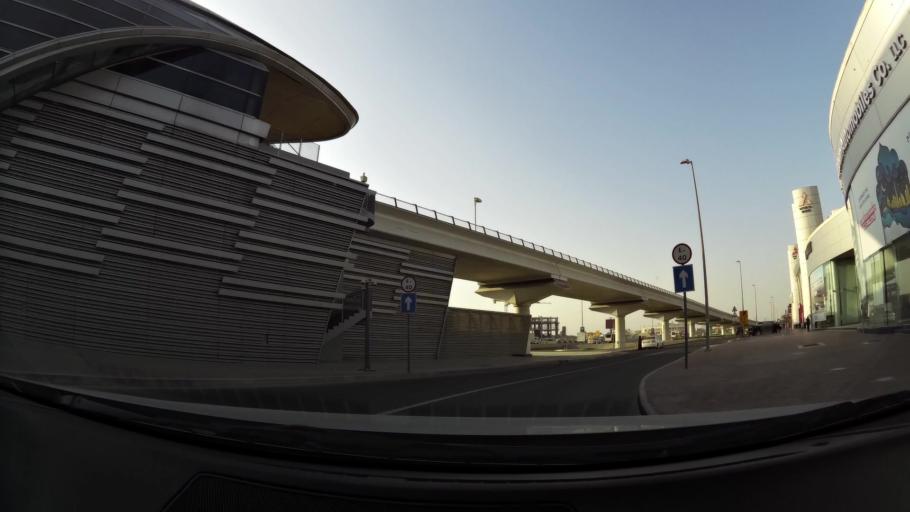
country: AE
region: Dubai
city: Dubai
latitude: 25.1560
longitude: 55.2289
